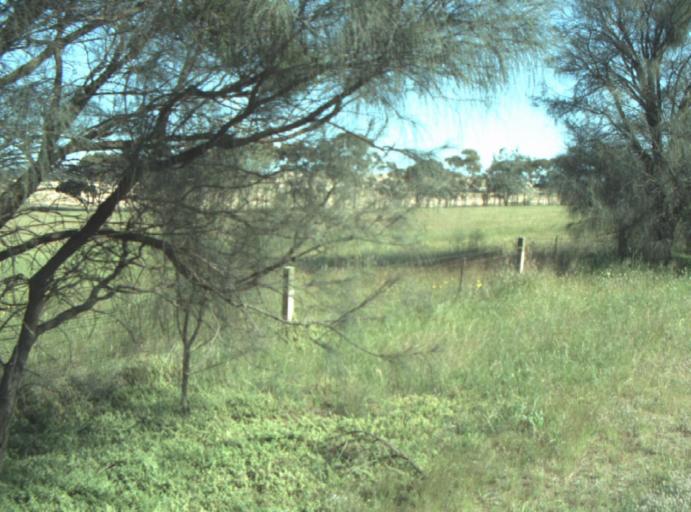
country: AU
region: Victoria
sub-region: Greater Geelong
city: Lara
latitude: -37.9279
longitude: 144.3951
